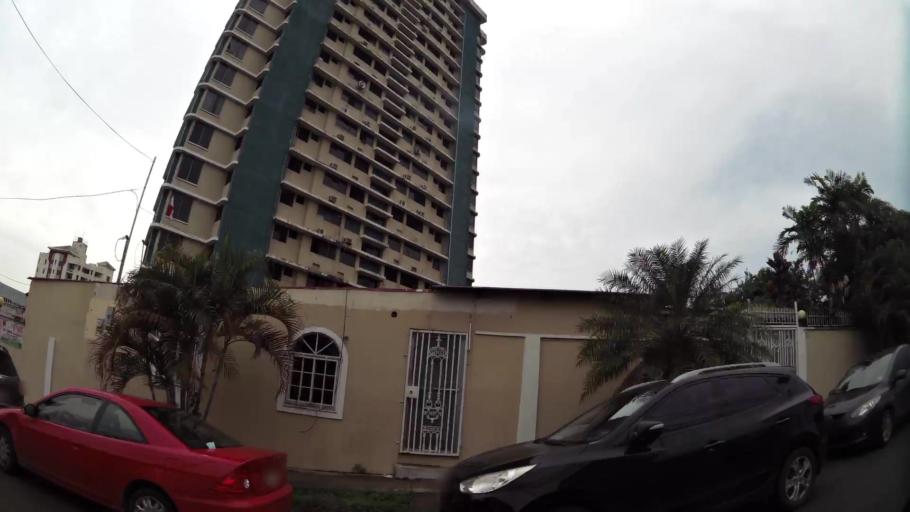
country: PA
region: Panama
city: Panama
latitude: 9.0168
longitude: -79.5207
